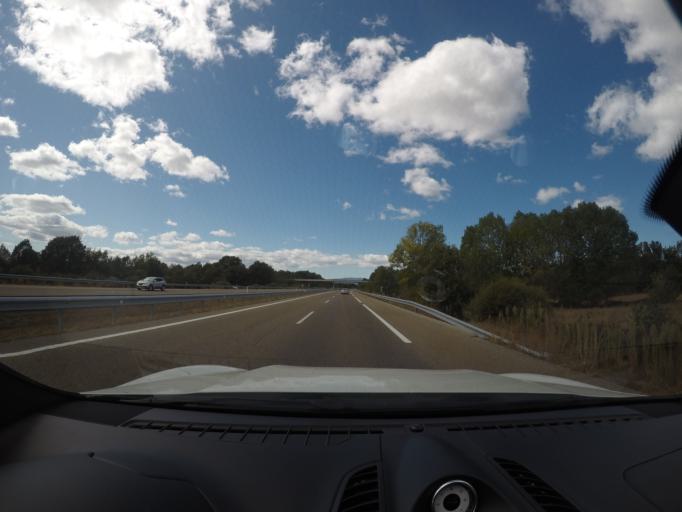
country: ES
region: Castille and Leon
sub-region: Provincia de Zamora
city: Asturianos
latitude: 42.0437
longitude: -6.4810
